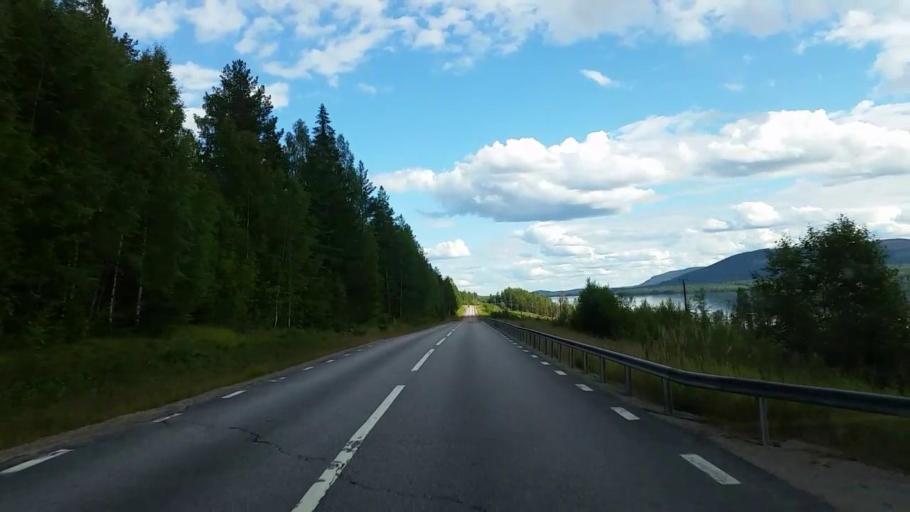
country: SE
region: Gaevleborg
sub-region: Ljusdals Kommun
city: Farila
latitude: 62.1092
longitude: 15.7693
